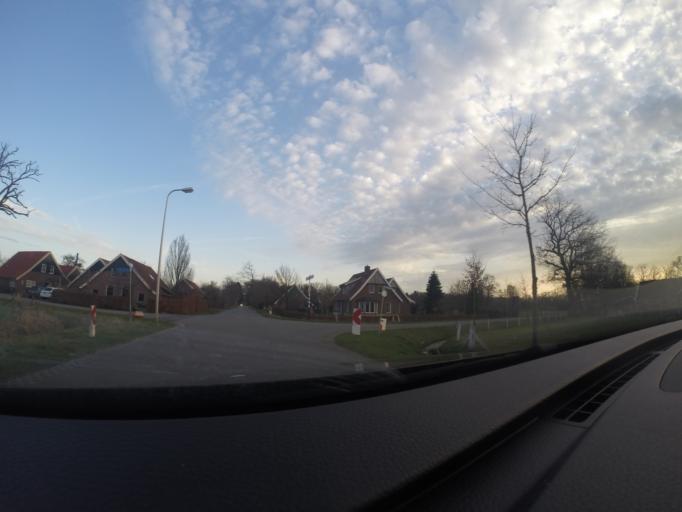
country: NL
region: Overijssel
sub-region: Gemeente Haaksbergen
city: Haaksbergen
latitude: 52.1473
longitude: 6.7448
